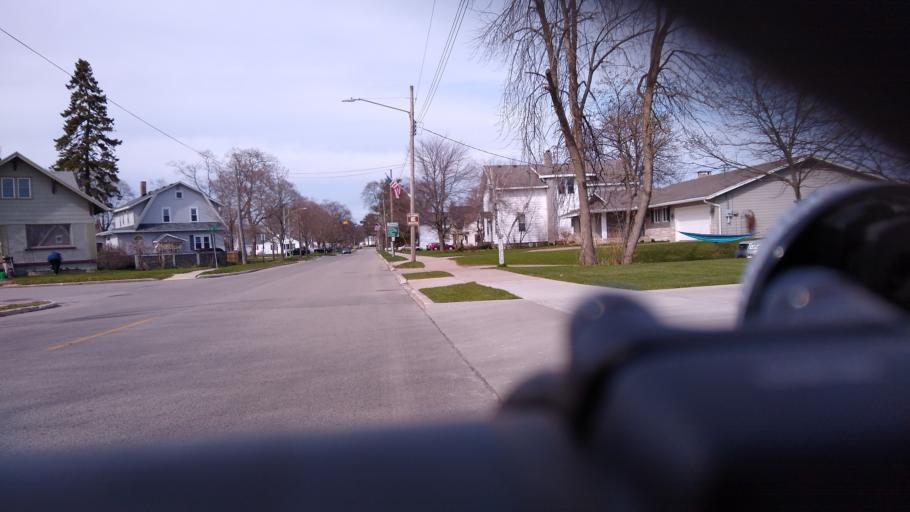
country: US
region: Michigan
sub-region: Delta County
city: Escanaba
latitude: 45.7338
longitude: -87.0619
